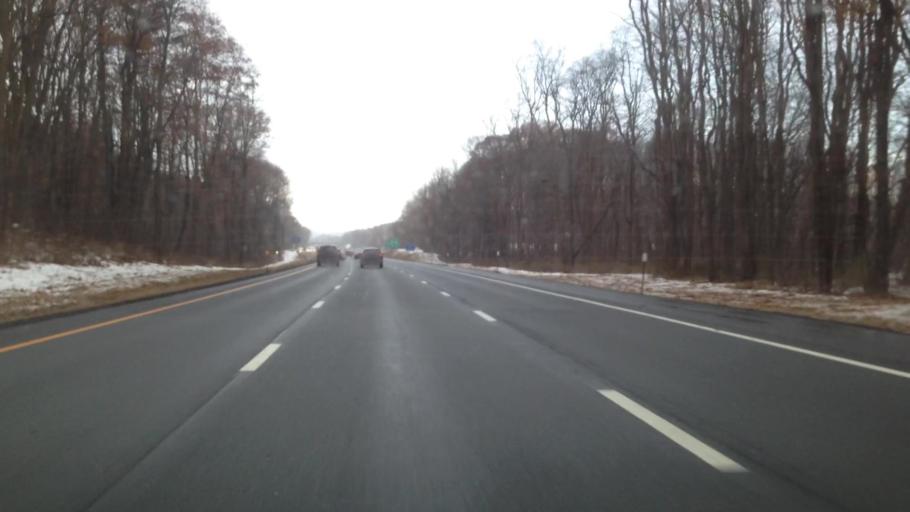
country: US
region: New York
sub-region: Schenectady County
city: Rotterdam
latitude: 42.7463
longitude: -73.9193
